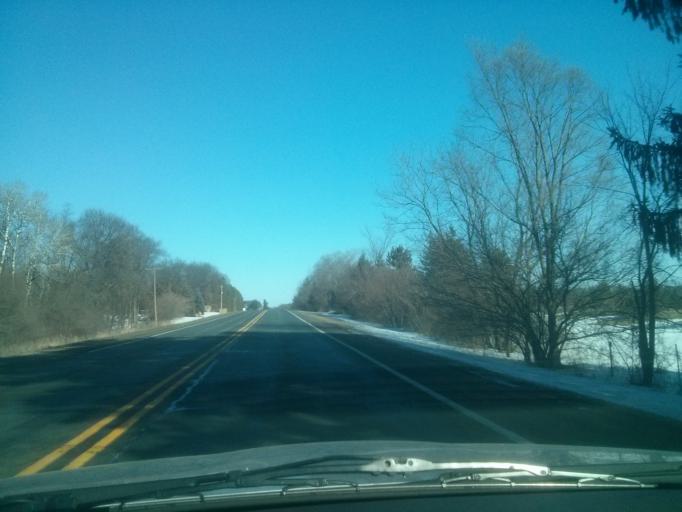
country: US
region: Minnesota
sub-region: Washington County
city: Bayport
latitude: 45.0499
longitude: -92.7410
